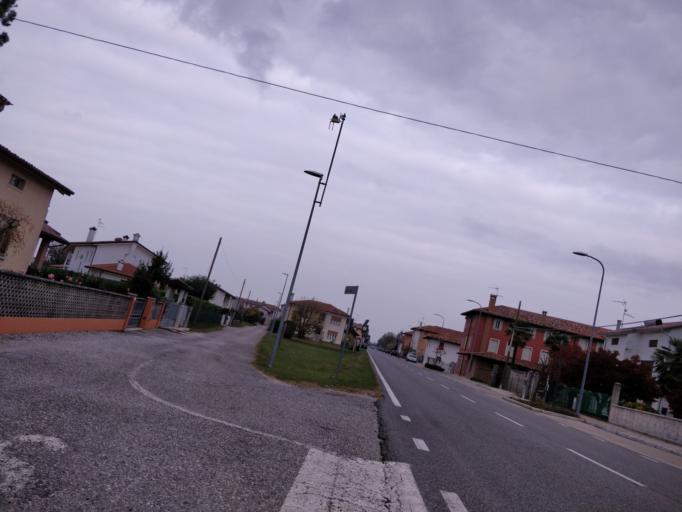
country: IT
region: Friuli Venezia Giulia
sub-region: Provincia di Udine
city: Bertiolo
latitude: 45.9460
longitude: 13.0554
